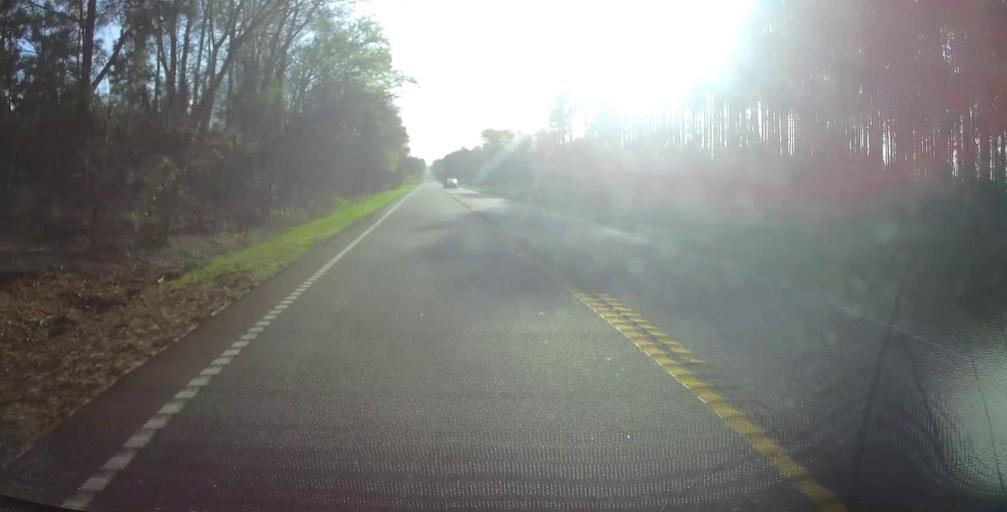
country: US
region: Georgia
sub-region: Tattnall County
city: Reidsville
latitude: 32.1336
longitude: -82.0453
